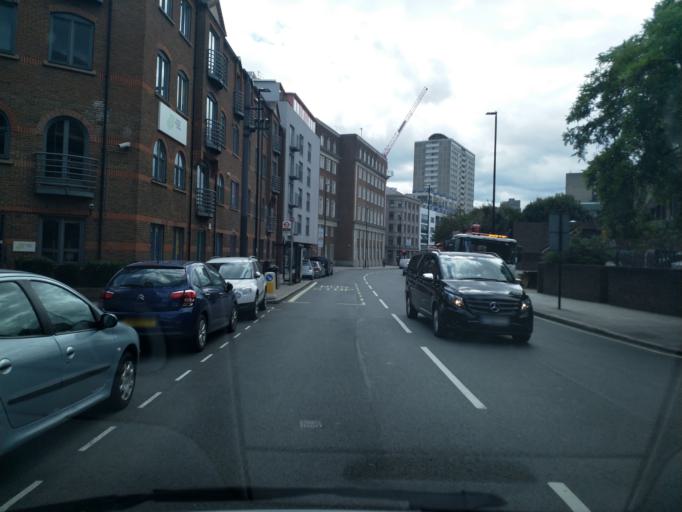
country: GB
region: England
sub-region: Greater London
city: Islington
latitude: 51.5295
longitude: -0.1020
